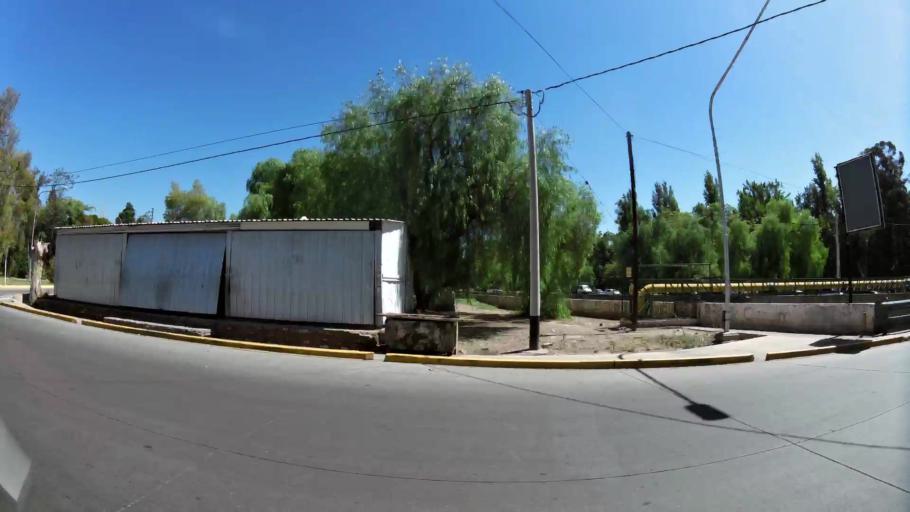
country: AR
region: Mendoza
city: Mendoza
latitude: -32.9016
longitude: -68.8663
